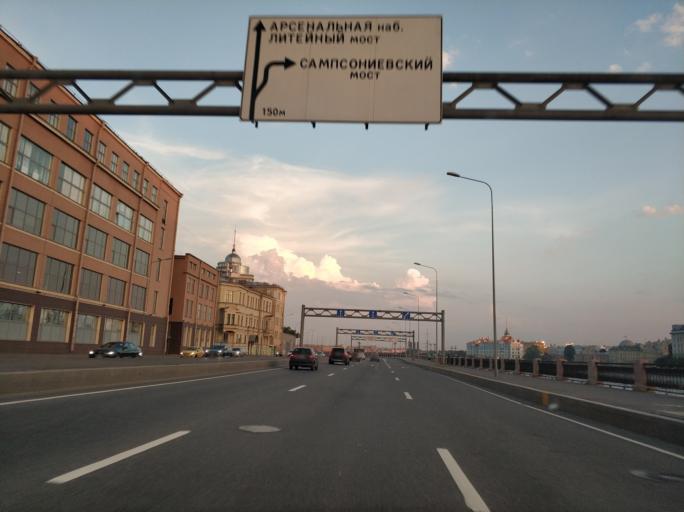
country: RU
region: Leningrad
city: Sampsonievskiy
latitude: 59.9620
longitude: 30.3379
